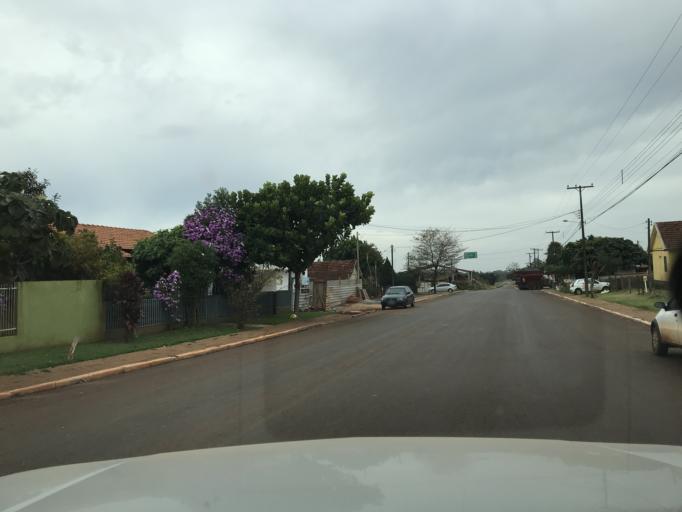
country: BR
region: Parana
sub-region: Marechal Candido Rondon
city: Marechal Candido Rondon
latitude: -24.4686
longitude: -53.9593
